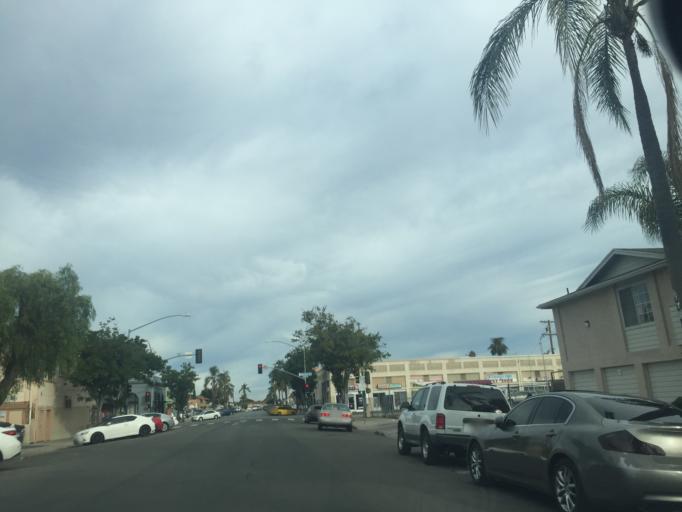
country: US
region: California
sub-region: San Diego County
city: San Diego
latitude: 32.7490
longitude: -117.1032
